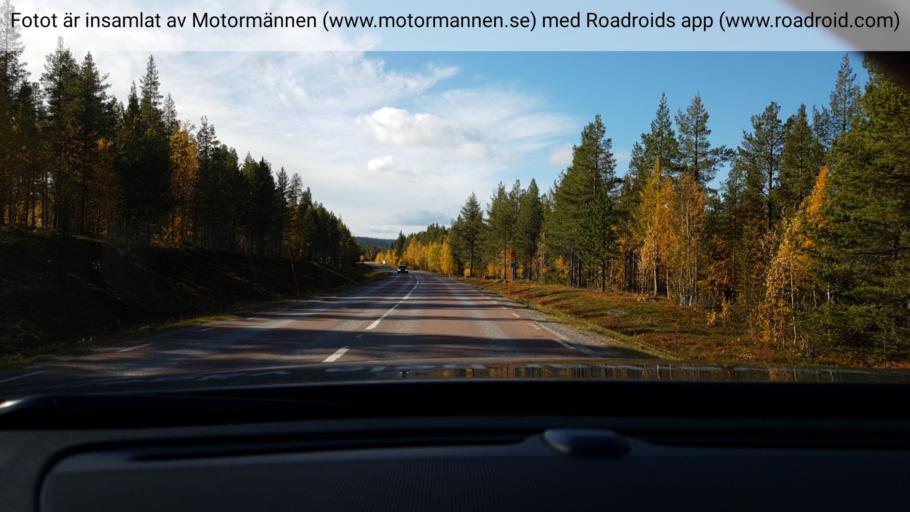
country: SE
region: Norrbotten
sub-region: Arjeplogs Kommun
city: Arjeplog
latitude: 66.0588
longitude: 17.9386
